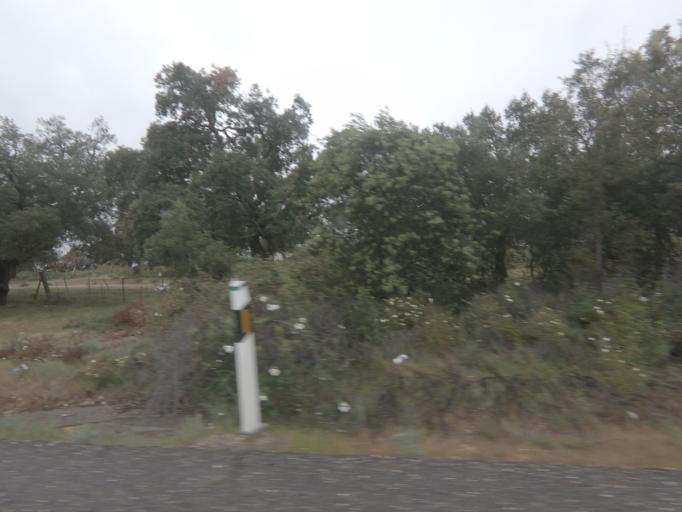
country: ES
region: Extremadura
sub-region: Provincia de Badajoz
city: Puebla de Obando
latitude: 39.1554
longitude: -6.6456
